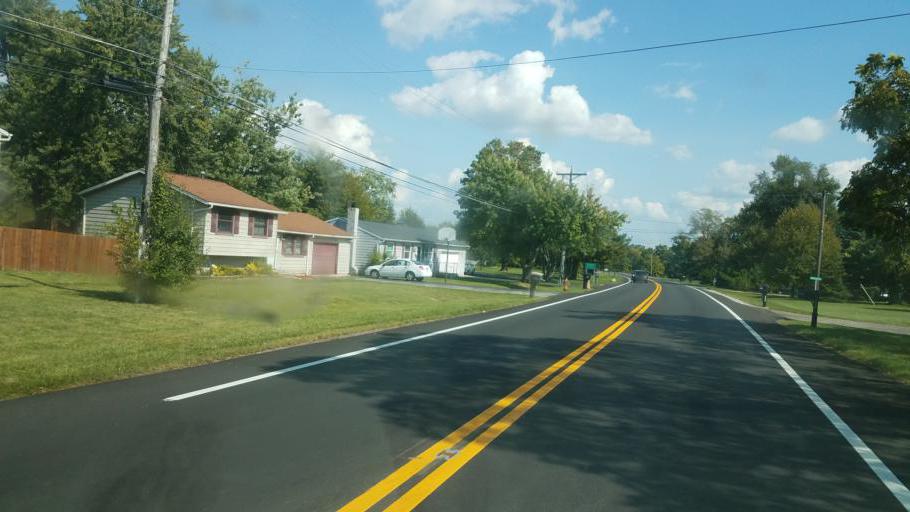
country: US
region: Ohio
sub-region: Franklin County
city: Grove City
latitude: 39.9157
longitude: -83.0902
